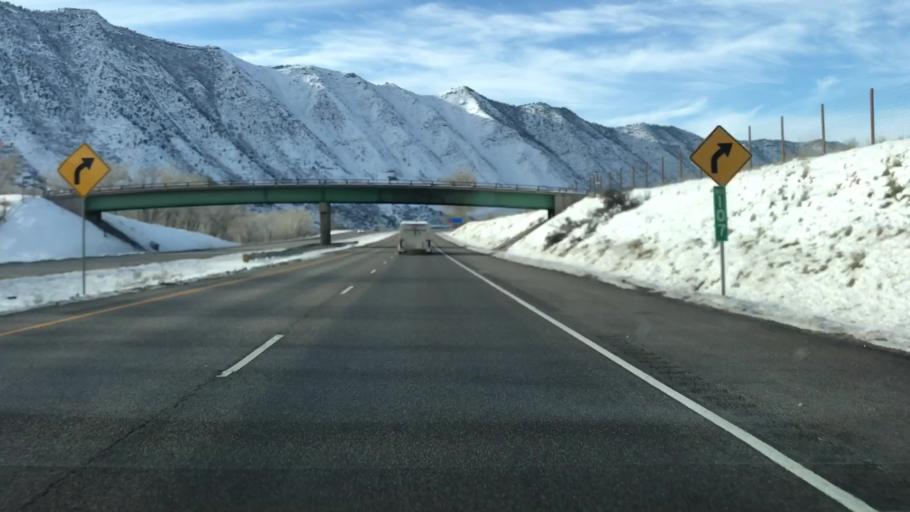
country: US
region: Colorado
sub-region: Garfield County
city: New Castle
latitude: 39.5696
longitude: -107.4854
